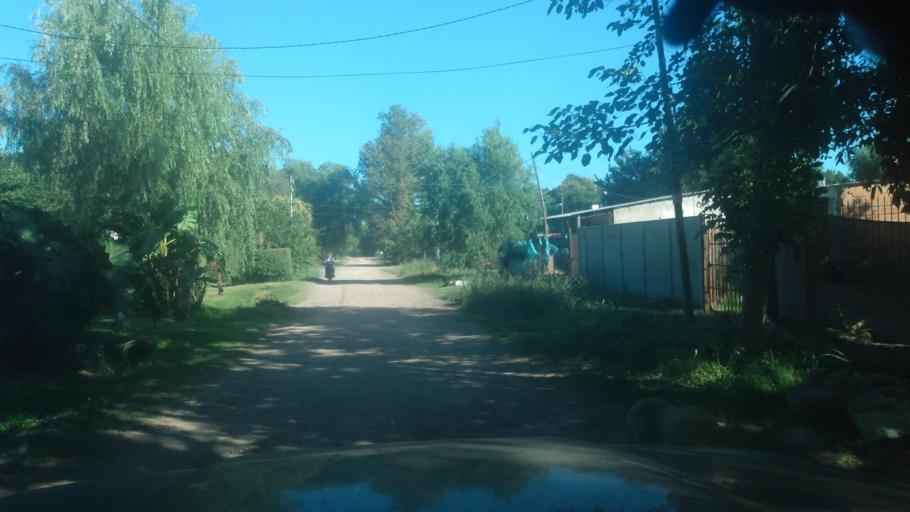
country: AR
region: Buenos Aires
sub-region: Partido de Lujan
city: Lujan
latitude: -34.5861
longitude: -59.0611
